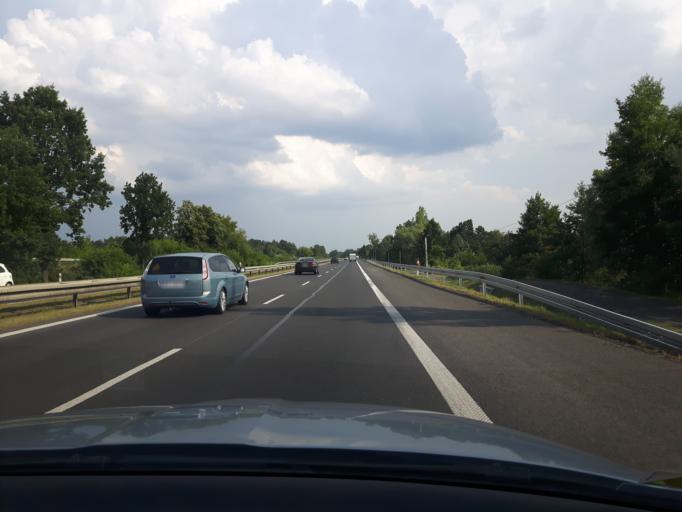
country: PL
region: Masovian Voivodeship
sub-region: Powiat nowodworski
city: Nowy Dwor Mazowiecki
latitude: 52.3980
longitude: 20.7145
